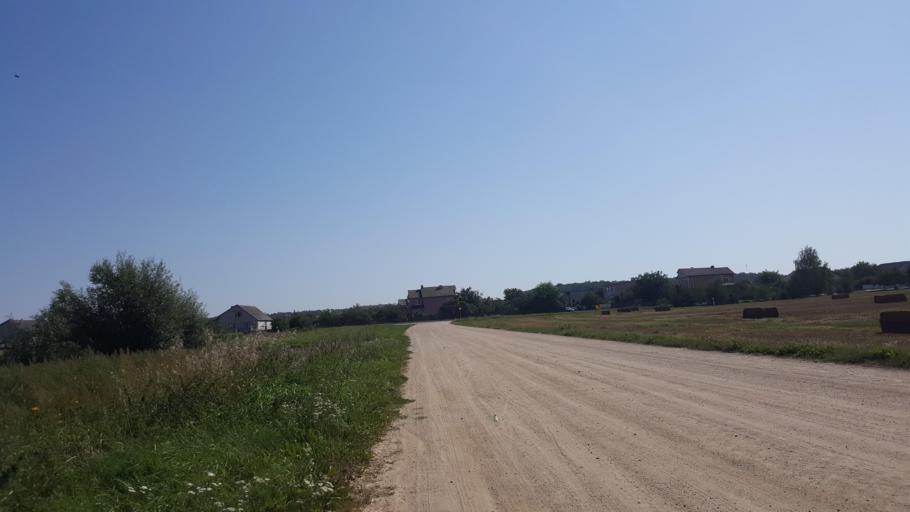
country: BY
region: Brest
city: Vysokaye
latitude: 52.4036
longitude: 23.4517
